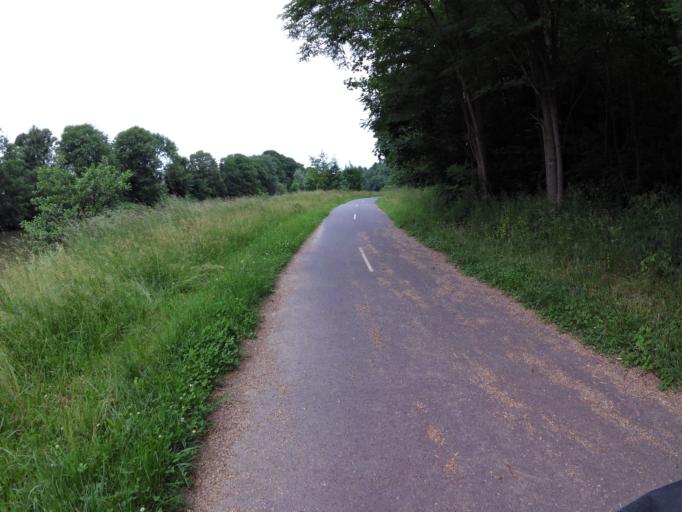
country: FR
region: Champagne-Ardenne
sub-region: Departement des Ardennes
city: Charleville-Mezieres
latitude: 49.7666
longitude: 4.7297
